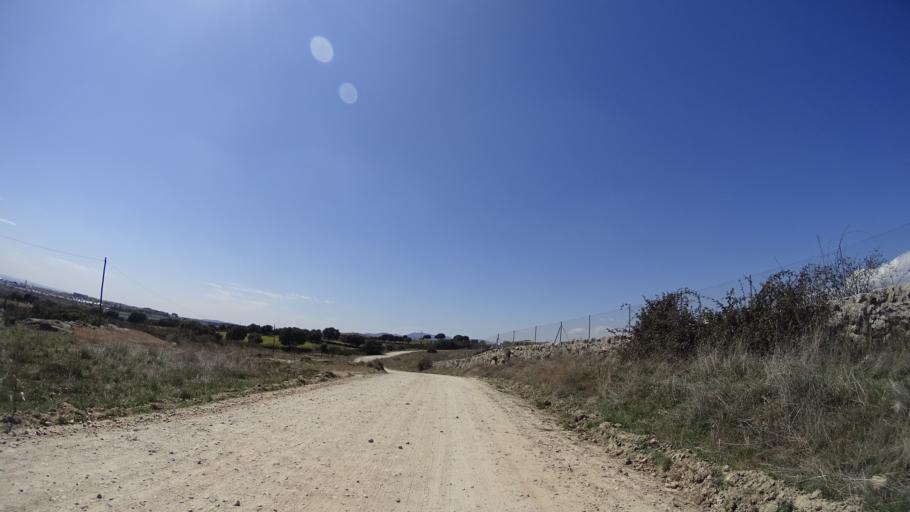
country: ES
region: Madrid
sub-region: Provincia de Madrid
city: Colmenar Viejo
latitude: 40.6874
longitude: -3.7581
